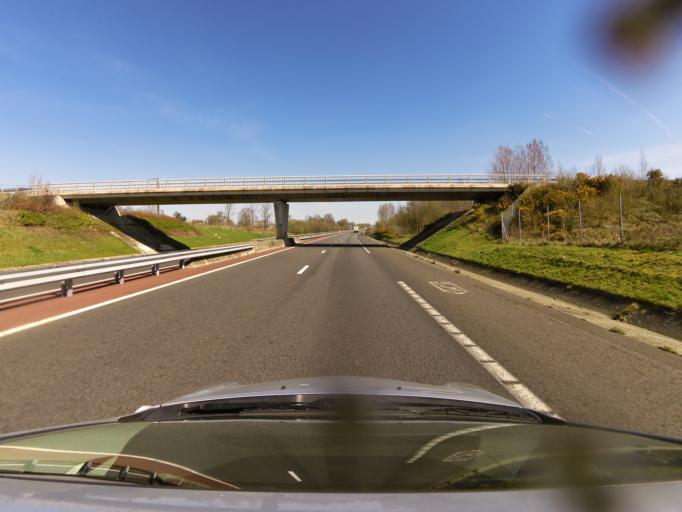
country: FR
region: Lower Normandy
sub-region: Departement de la Manche
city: Villedieu-les-Poeles
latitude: 48.7748
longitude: -1.2744
